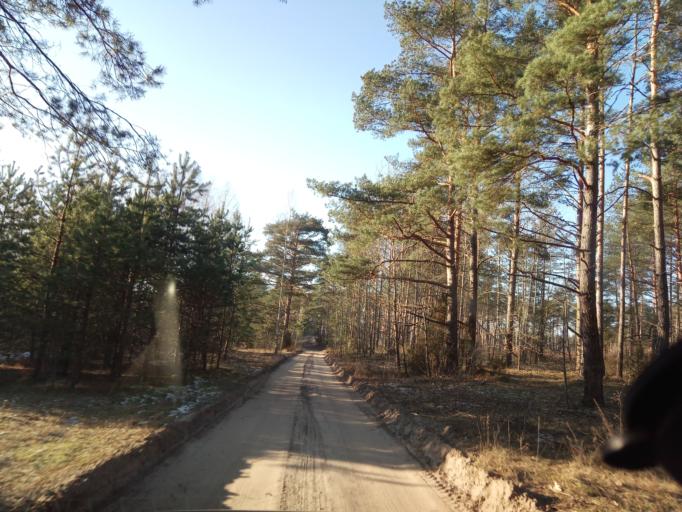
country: LT
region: Alytaus apskritis
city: Druskininkai
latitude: 53.9567
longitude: 23.8865
